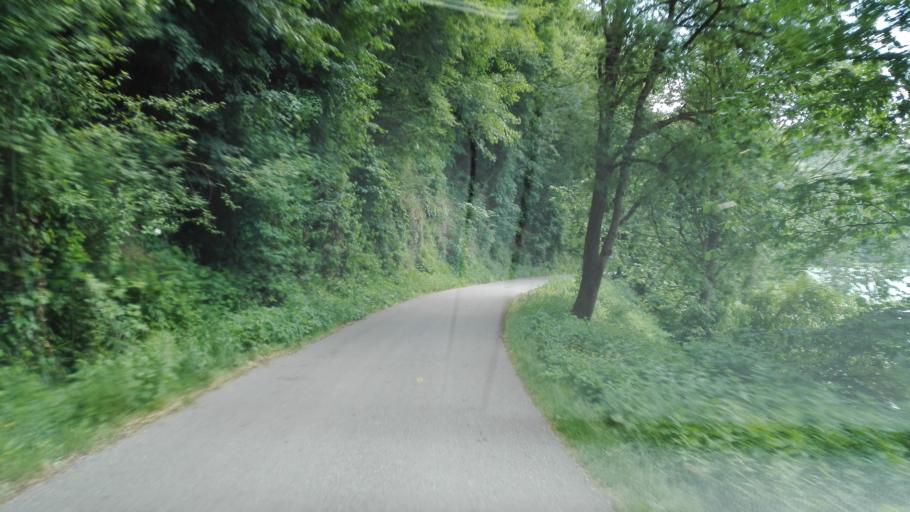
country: AT
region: Upper Austria
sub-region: Politischer Bezirk Rohrbach
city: Atzesberg
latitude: 48.4321
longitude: 13.8754
